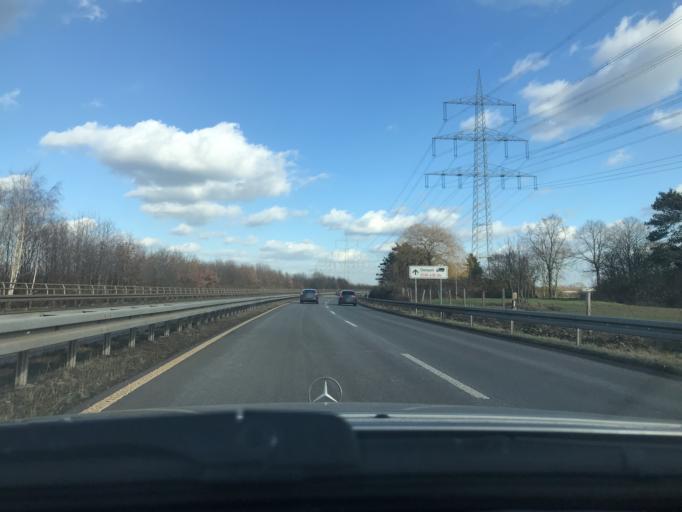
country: DE
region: North Rhine-Westphalia
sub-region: Regierungsbezirk Dusseldorf
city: Moers
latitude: 51.3870
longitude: 6.6671
